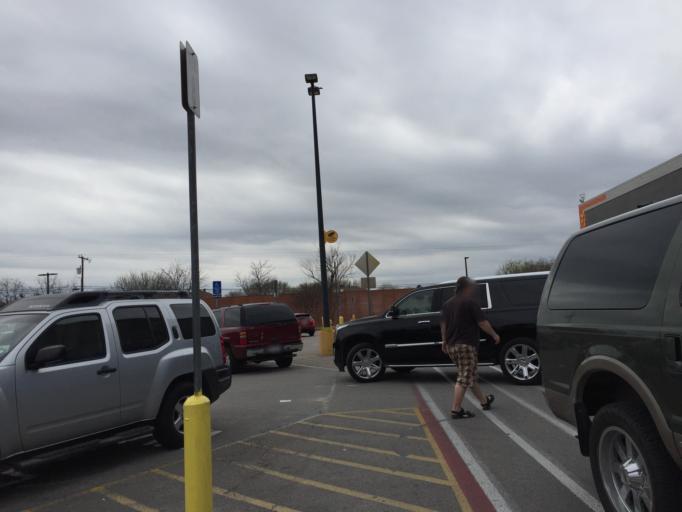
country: US
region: Texas
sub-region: Bell County
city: Harker Heights
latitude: 31.0695
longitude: -97.6738
